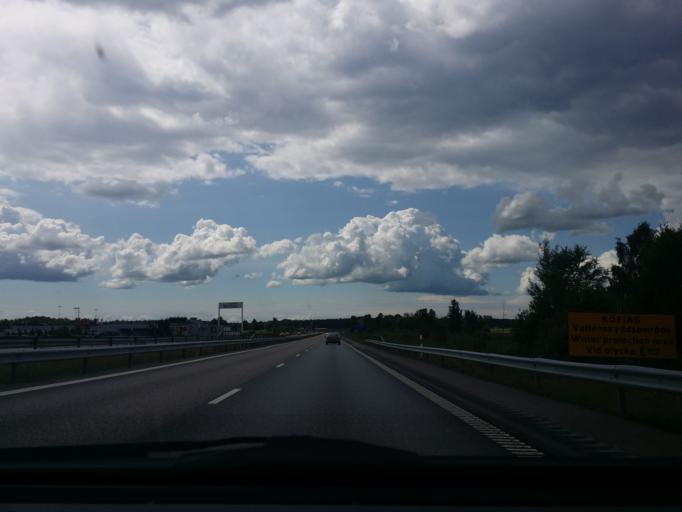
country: SE
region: Vaestmanland
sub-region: Kopings Kommun
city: Koping
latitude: 59.5265
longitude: 15.9764
